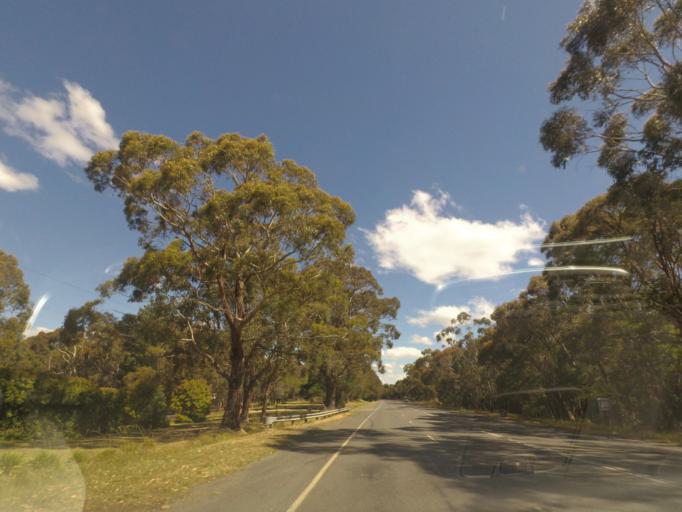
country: AU
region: Victoria
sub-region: Hume
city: Sunbury
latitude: -37.4244
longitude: 144.5541
